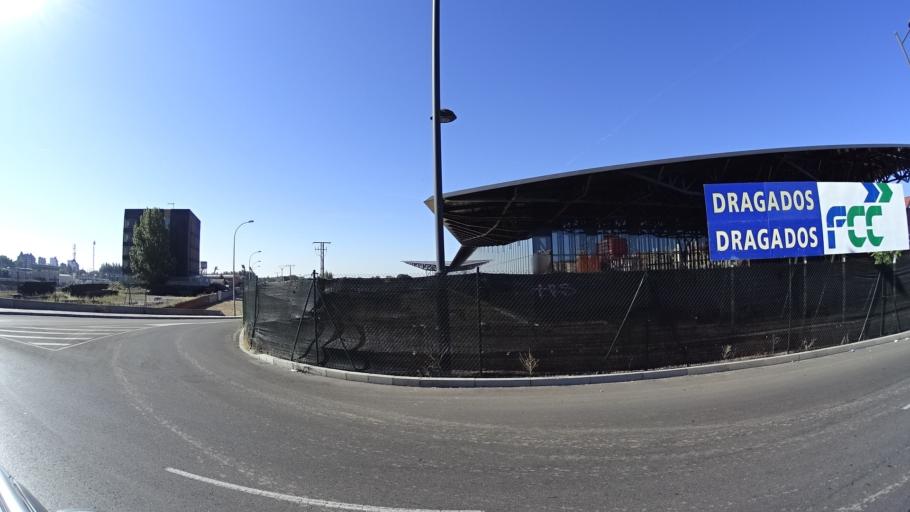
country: ES
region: Castille and Leon
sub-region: Provincia de Leon
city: Leon
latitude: 42.5948
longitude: -5.5834
